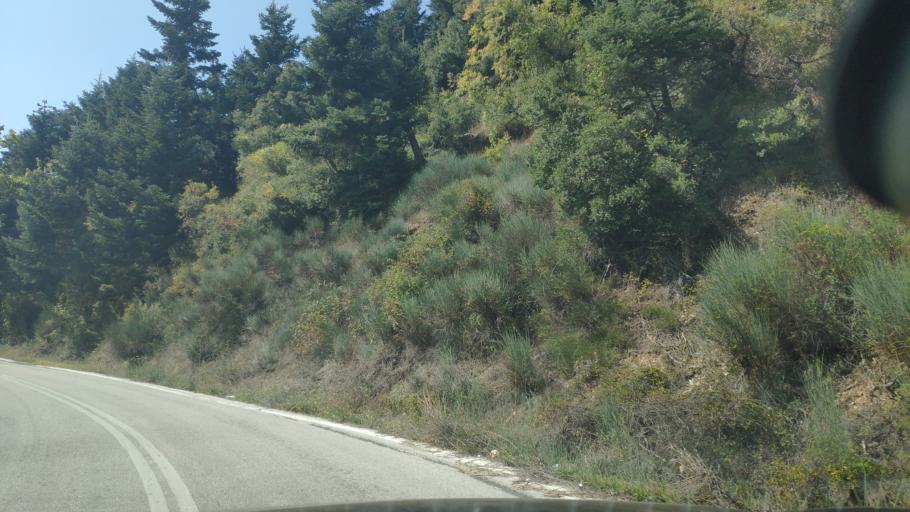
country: GR
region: West Greece
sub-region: Nomos Achaias
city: Aiyira
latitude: 37.8668
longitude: 22.3746
